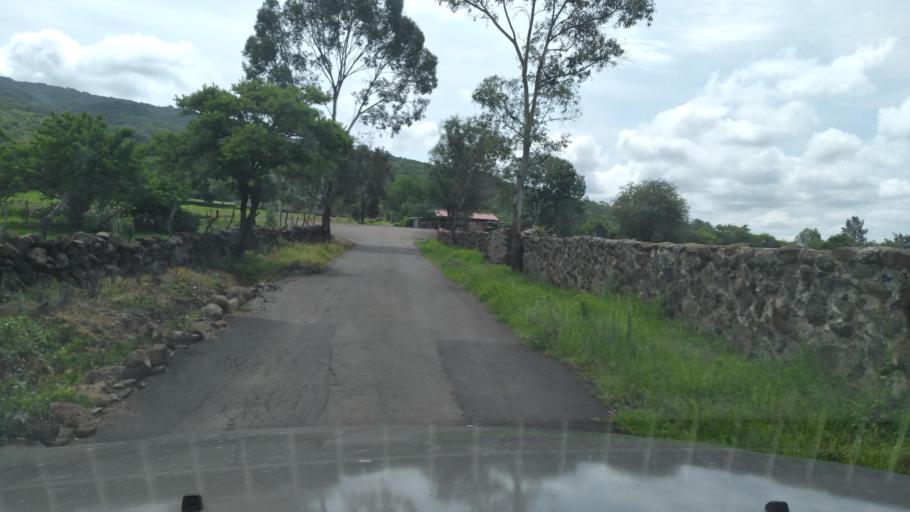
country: MX
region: Jalisco
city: Capilla de Guadalupe
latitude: 20.7469
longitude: -102.6241
